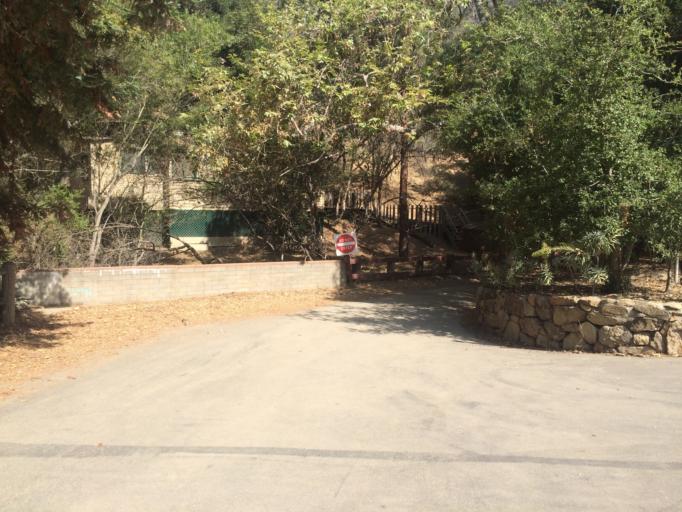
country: US
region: California
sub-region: Los Angeles County
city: Santa Monica
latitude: 34.0542
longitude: -118.5289
